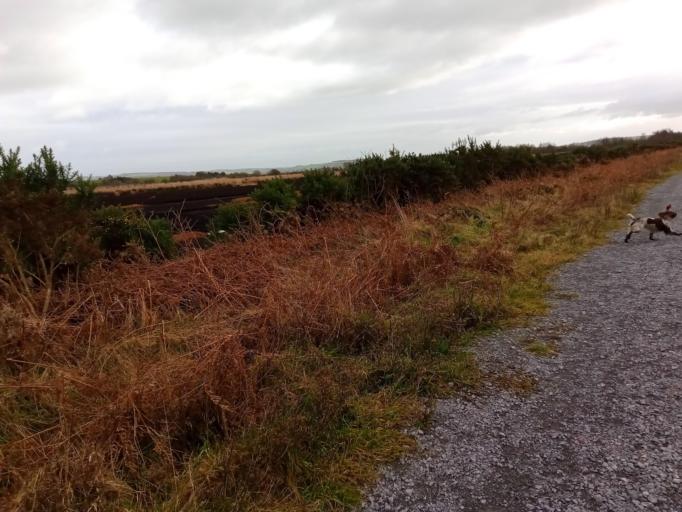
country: IE
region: Munster
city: Thurles
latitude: 52.5964
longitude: -7.7456
